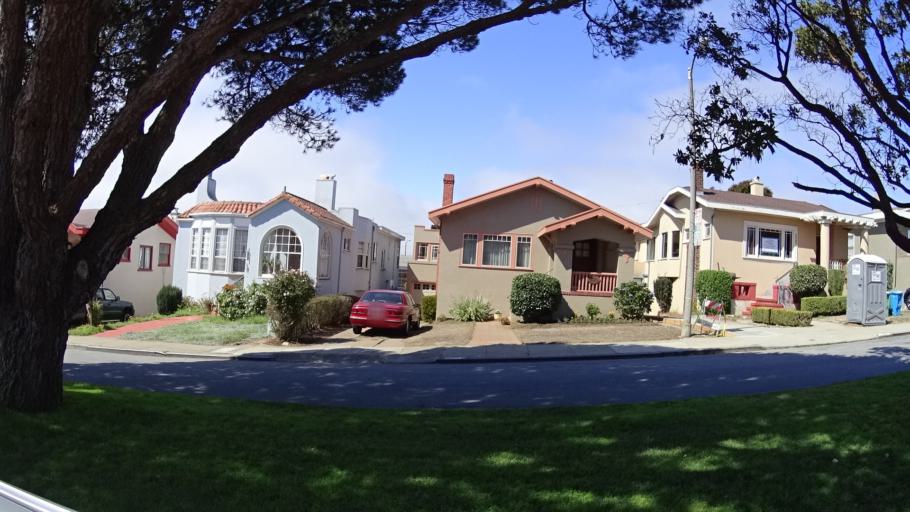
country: US
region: California
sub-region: San Mateo County
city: Daly City
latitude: 37.7262
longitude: -122.4581
